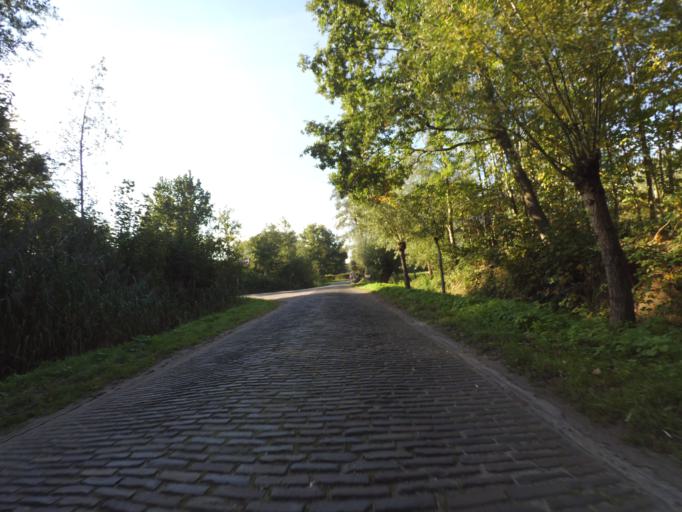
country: NL
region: Gelderland
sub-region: Gemeente Nijkerk
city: Nijkerk
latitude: 52.2440
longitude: 5.5307
